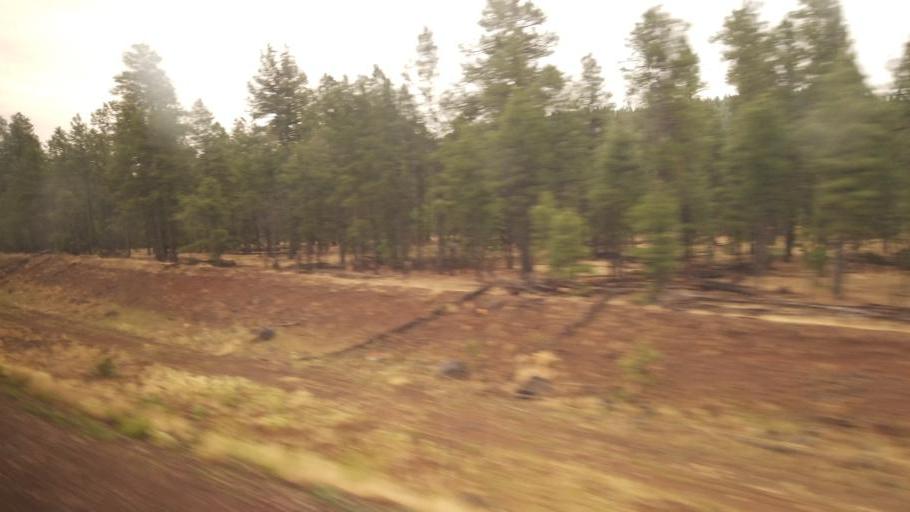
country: US
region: Arizona
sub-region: Coconino County
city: Parks
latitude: 35.2543
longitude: -111.9298
